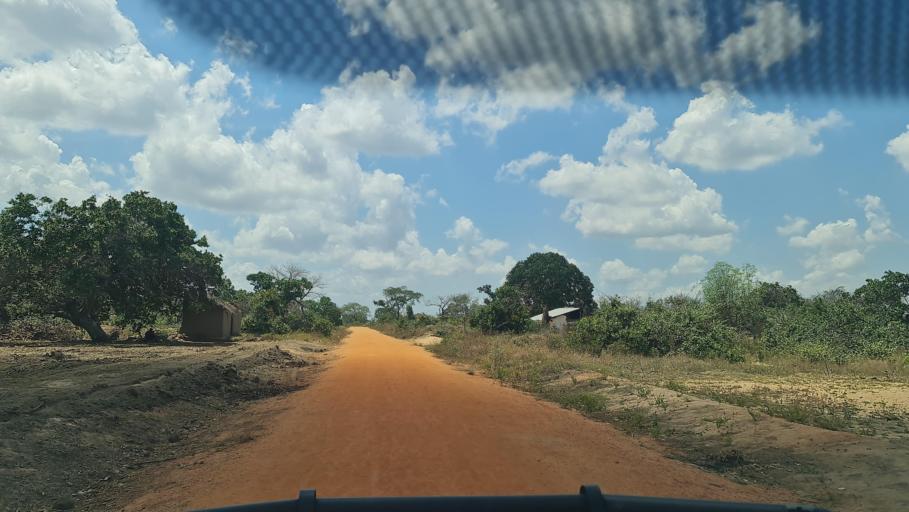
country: MZ
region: Nampula
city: Ilha de Mocambique
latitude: -15.0525
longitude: 40.3286
